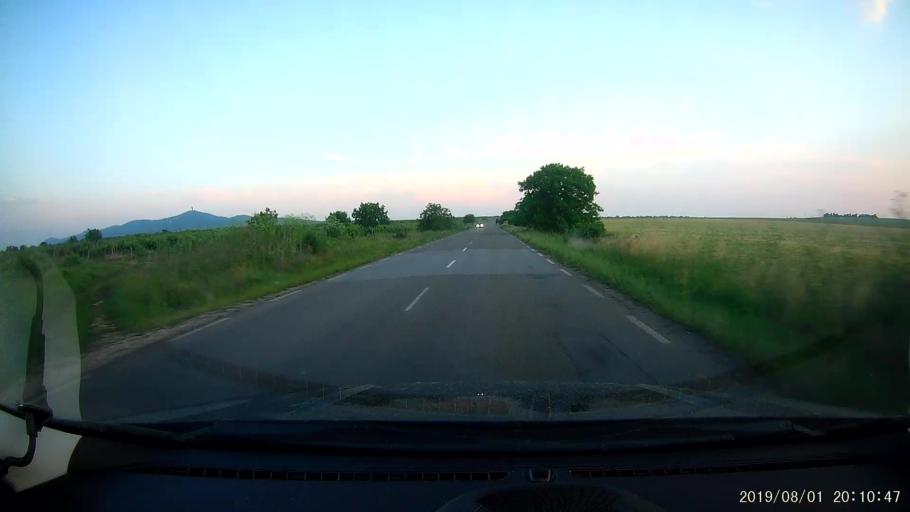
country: BG
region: Yambol
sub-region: Obshtina Yambol
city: Yambol
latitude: 42.4746
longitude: 26.6026
